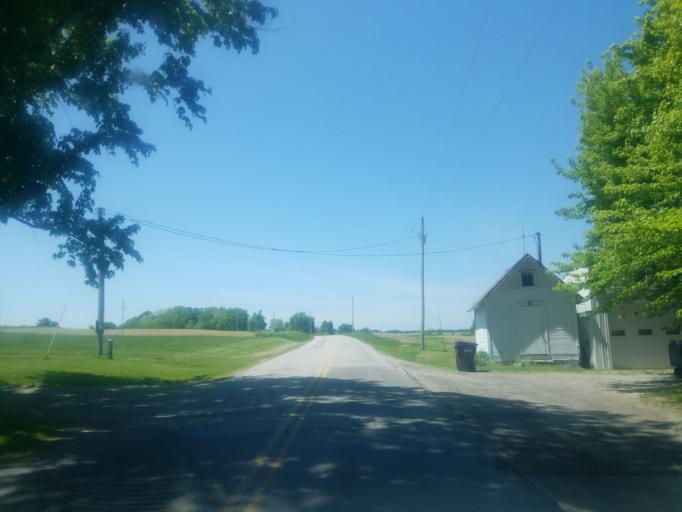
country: US
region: Ohio
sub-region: Huron County
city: New London
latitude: 41.1155
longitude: -82.4409
